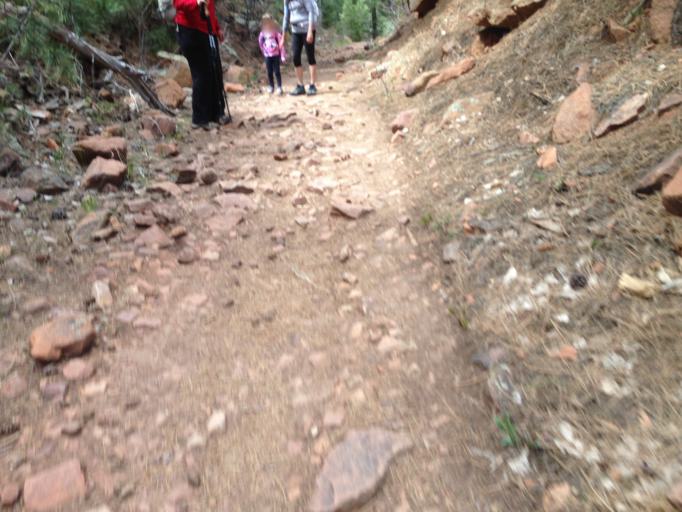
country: US
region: Colorado
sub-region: Boulder County
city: Boulder
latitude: 39.9274
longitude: -105.2775
